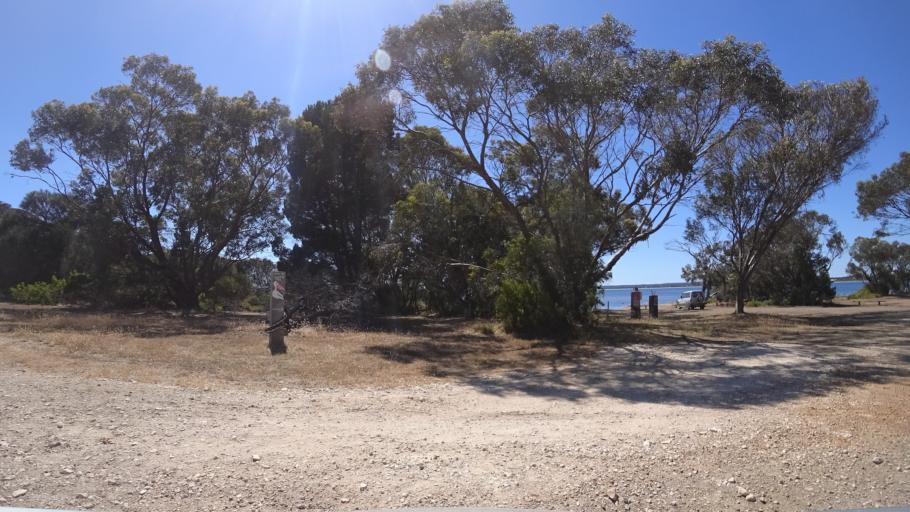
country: AU
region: South Australia
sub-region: Kangaroo Island
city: Kingscote
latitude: -35.7737
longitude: 137.7809
